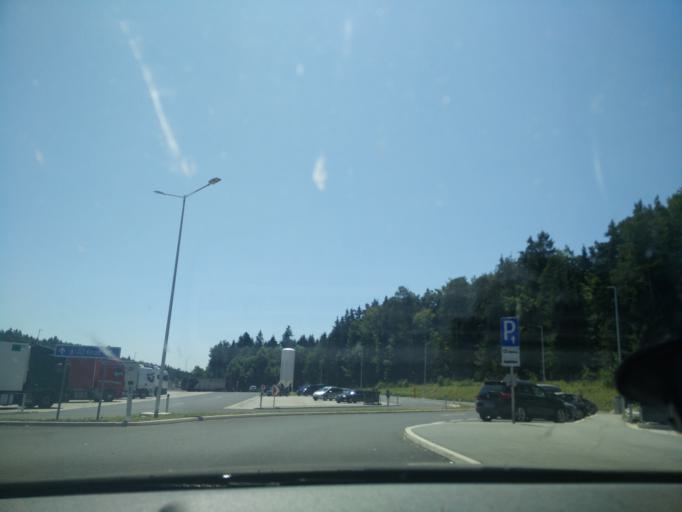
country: AT
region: Styria
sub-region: Politischer Bezirk Hartberg-Fuerstenfeld
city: Hainersdorf
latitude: 47.1190
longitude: 15.9834
